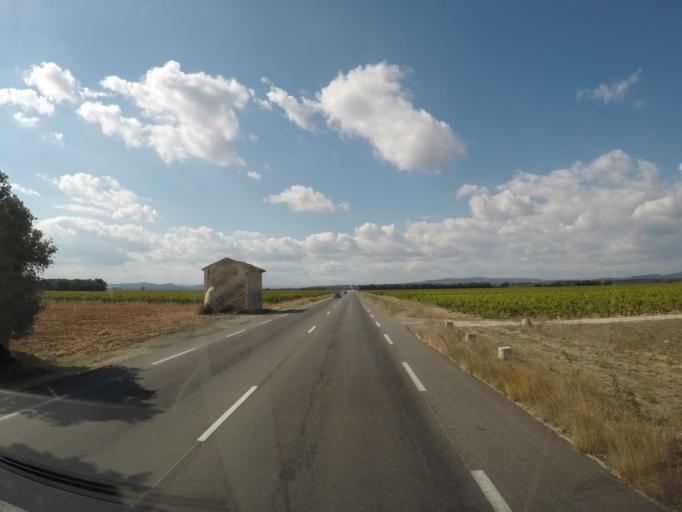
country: FR
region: Rhone-Alpes
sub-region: Departement de la Drome
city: Suze-la-Rousse
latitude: 44.2844
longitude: 4.8806
